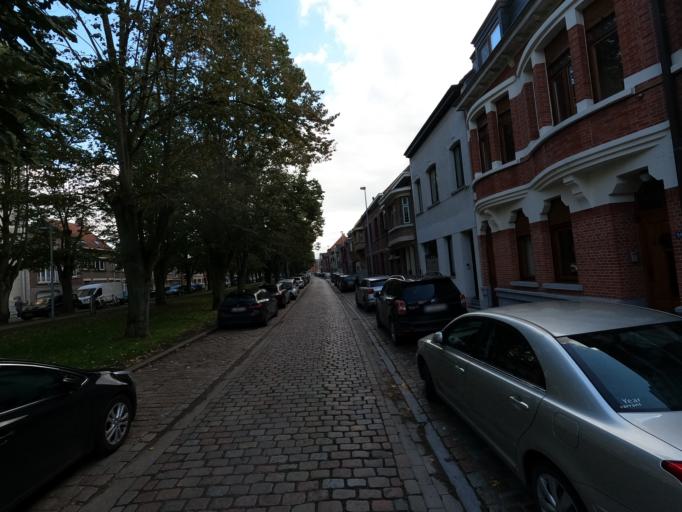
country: BE
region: Flanders
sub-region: Provincie Antwerpen
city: Herentals
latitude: 51.1757
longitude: 4.8315
